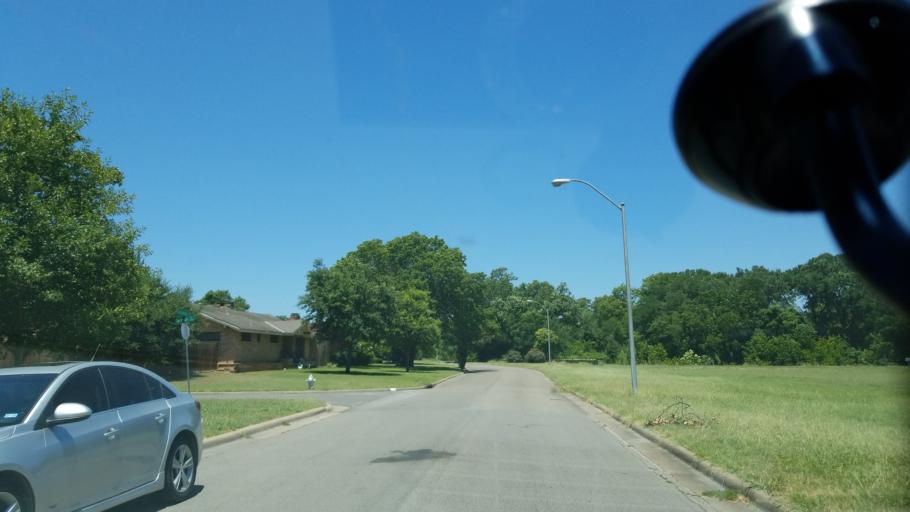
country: US
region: Texas
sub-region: Dallas County
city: Cockrell Hill
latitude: 32.6926
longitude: -96.8331
